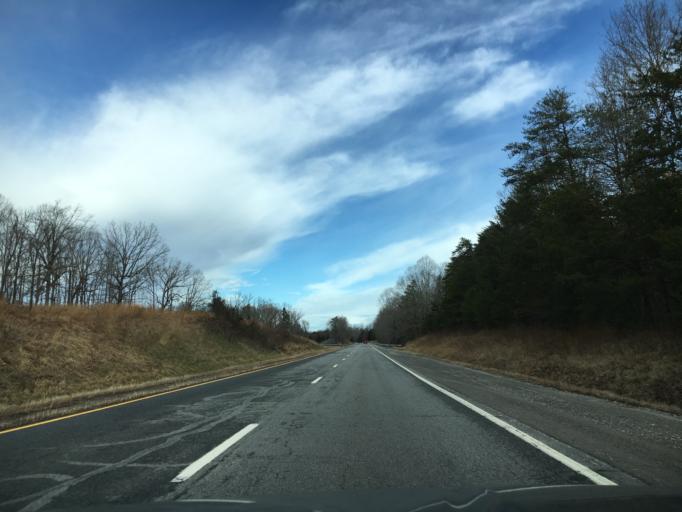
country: US
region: Virginia
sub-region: Nottoway County
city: Crewe
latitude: 37.2040
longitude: -78.2274
